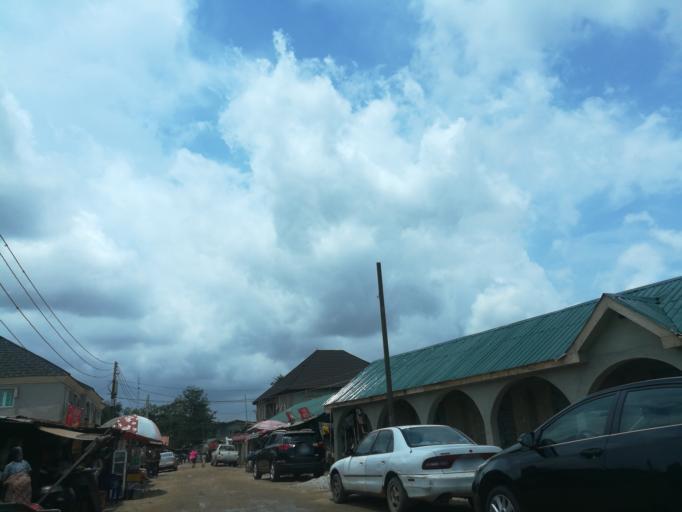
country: NG
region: Lagos
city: Somolu
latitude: 6.5426
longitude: 3.3608
